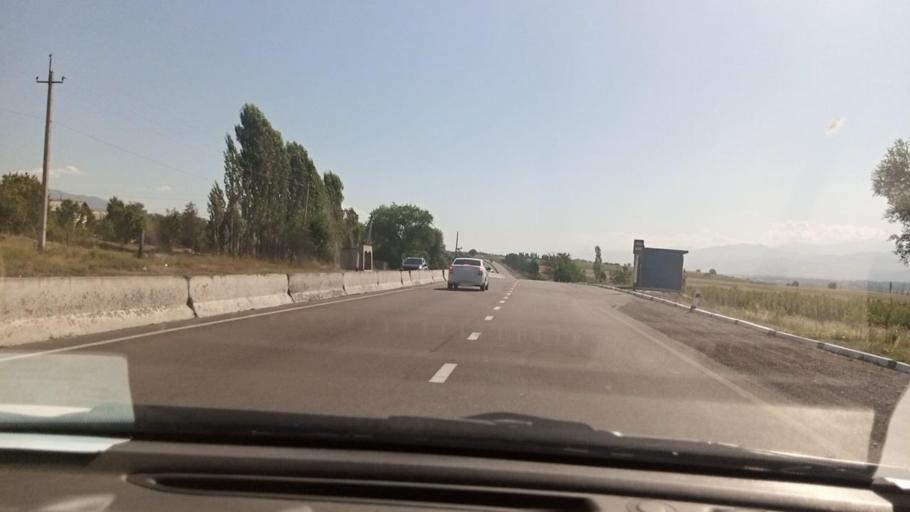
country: UZ
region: Toshkent
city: Angren
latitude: 40.9377
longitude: 69.8965
